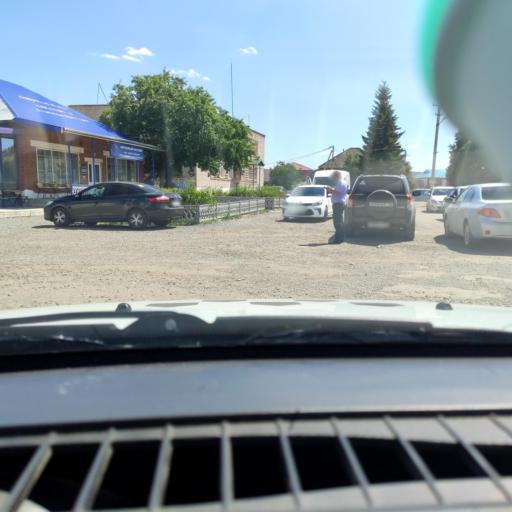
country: RU
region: Bashkortostan
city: Mesyagutovo
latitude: 55.5337
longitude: 58.2474
